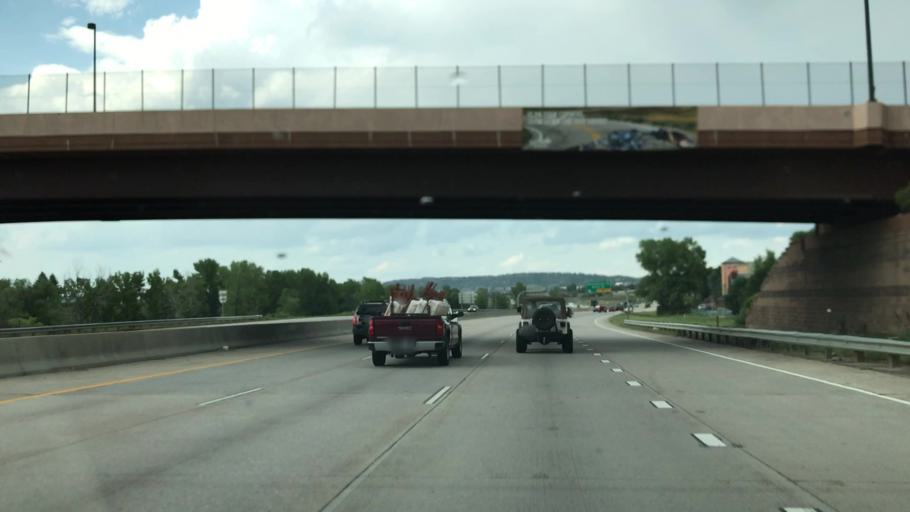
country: US
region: Colorado
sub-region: Douglas County
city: Castle Rock
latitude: 39.3741
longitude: -104.8630
